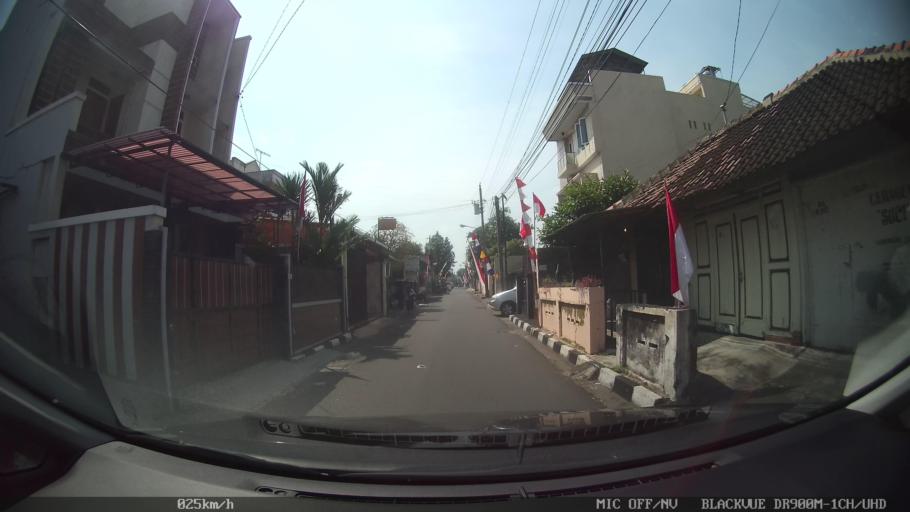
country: ID
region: Daerah Istimewa Yogyakarta
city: Yogyakarta
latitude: -7.7852
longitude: 110.3637
